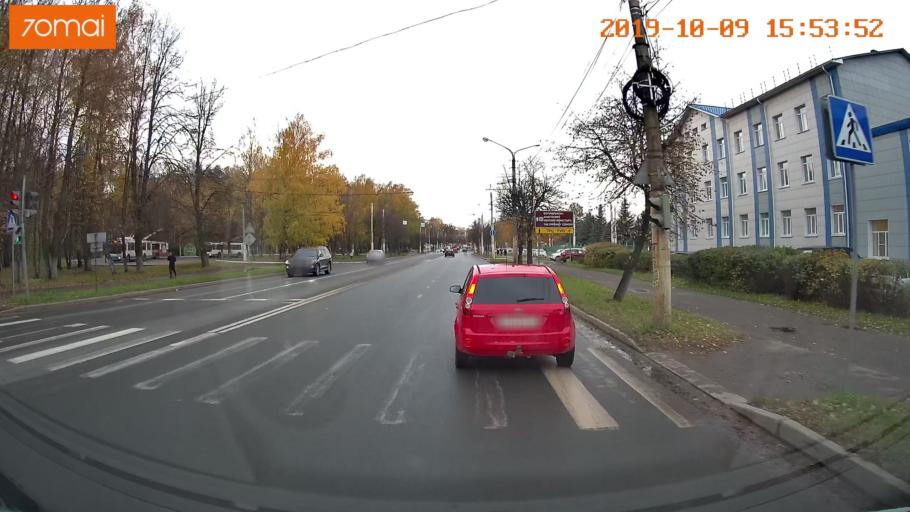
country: RU
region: Kostroma
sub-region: Kostromskoy Rayon
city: Kostroma
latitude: 57.7842
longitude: 40.9602
